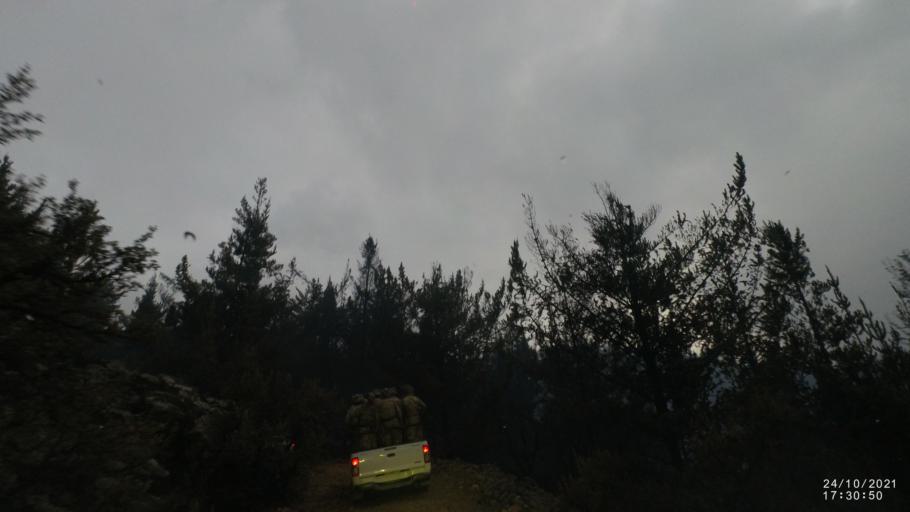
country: BO
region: Cochabamba
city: Cochabamba
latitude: -17.3230
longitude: -66.1293
